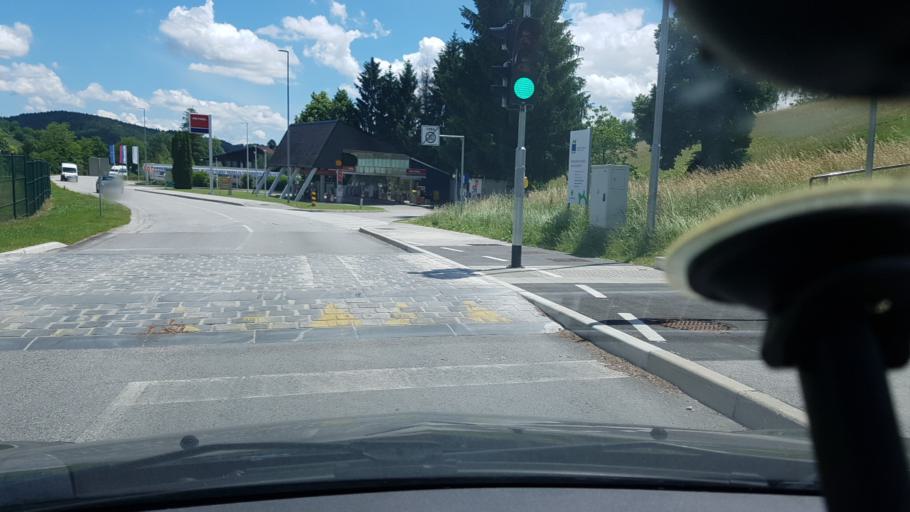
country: SI
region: Zrece
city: Zrece
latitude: 46.3724
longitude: 15.3897
